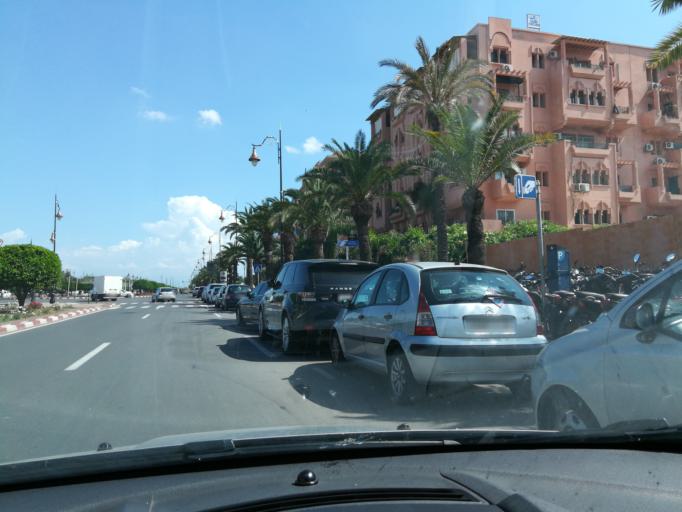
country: MA
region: Marrakech-Tensift-Al Haouz
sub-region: Marrakech
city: Marrakesh
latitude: 31.6206
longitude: -8.0101
